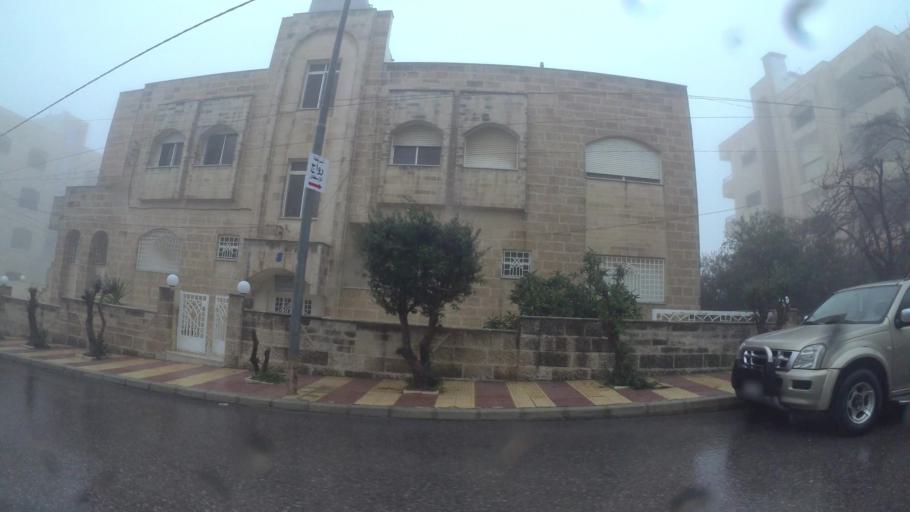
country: JO
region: Amman
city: Al Jubayhah
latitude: 32.0058
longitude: 35.8910
